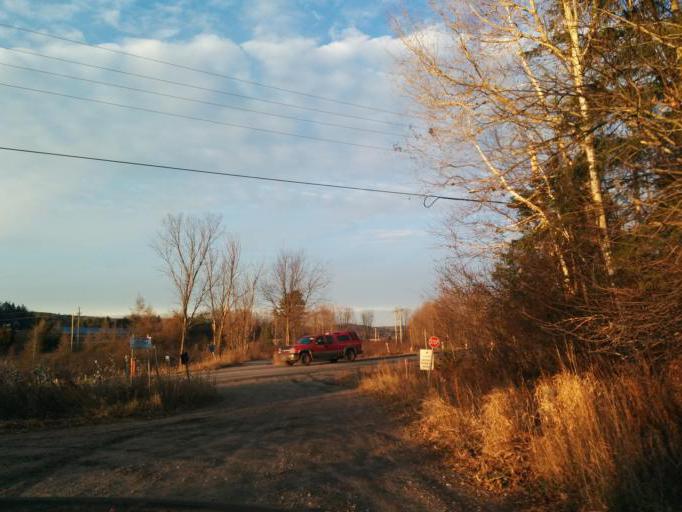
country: CA
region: Ontario
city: Bancroft
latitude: 45.0397
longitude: -78.5235
